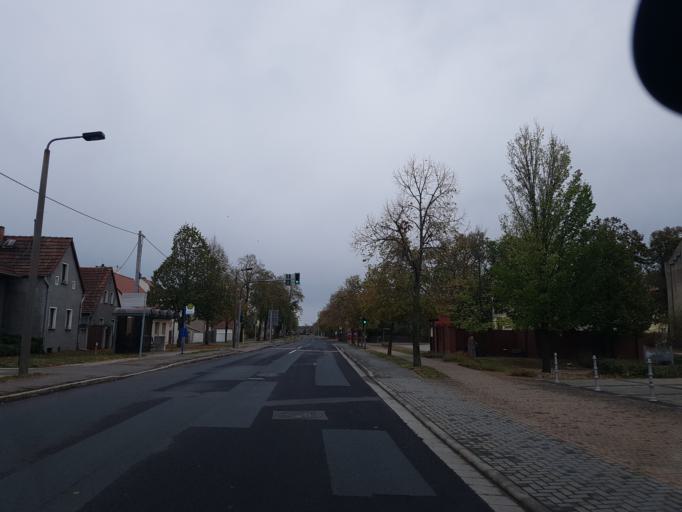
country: DE
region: Brandenburg
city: Falkenberg
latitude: 51.5884
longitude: 13.2360
